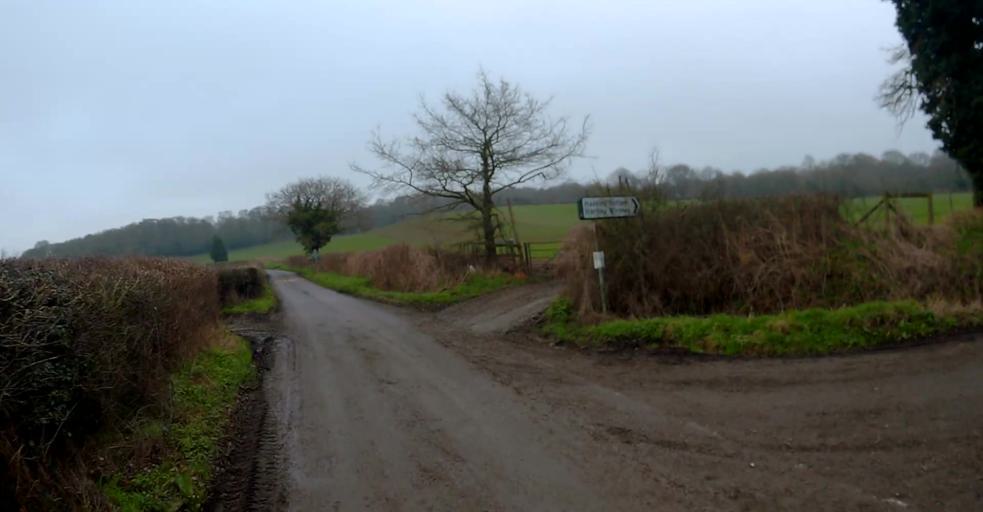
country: GB
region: England
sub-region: Hampshire
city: Hook
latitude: 51.3197
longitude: -0.9362
